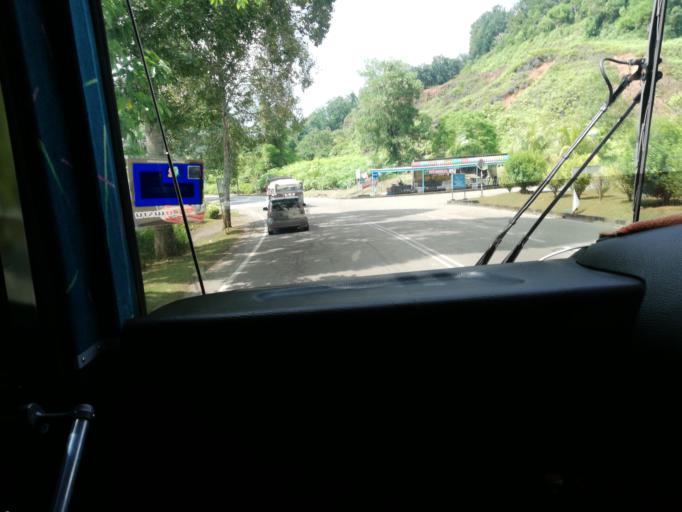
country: MY
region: Penang
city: Nibong Tebal
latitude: 5.2182
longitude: 100.6095
